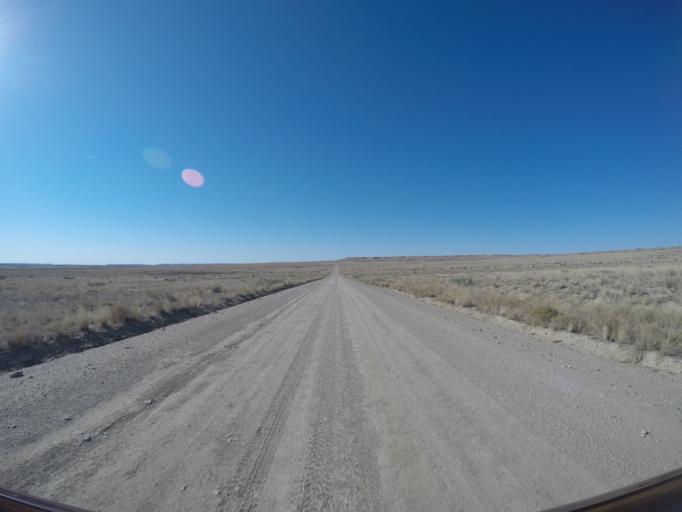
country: US
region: Colorado
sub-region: Otero County
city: La Junta
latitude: 37.7768
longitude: -103.5502
